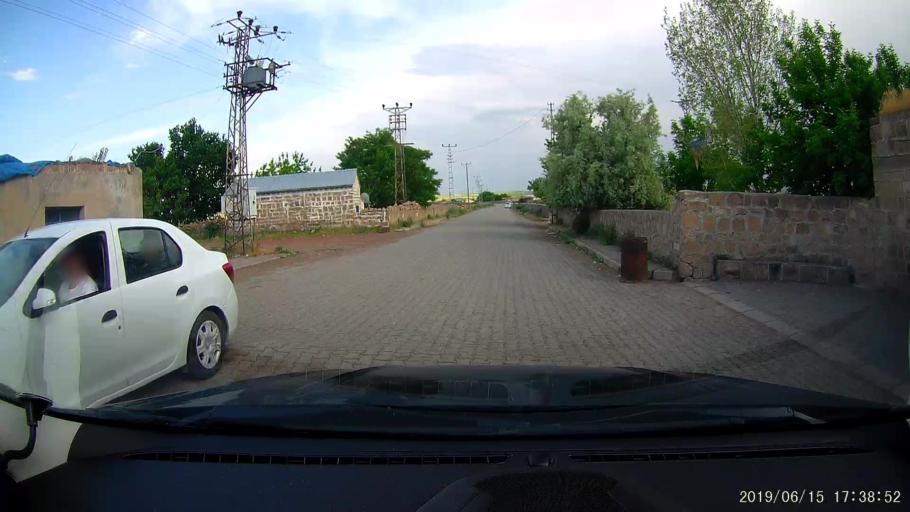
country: TR
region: Kars
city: Basgedikler
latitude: 40.5188
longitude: 43.5684
